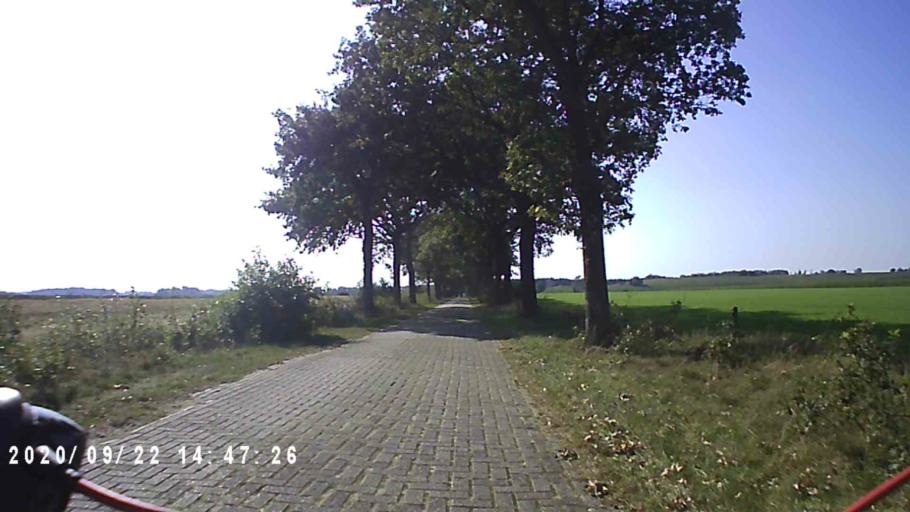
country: NL
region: Groningen
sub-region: Gemeente Leek
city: Leek
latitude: 53.0125
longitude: 6.3509
